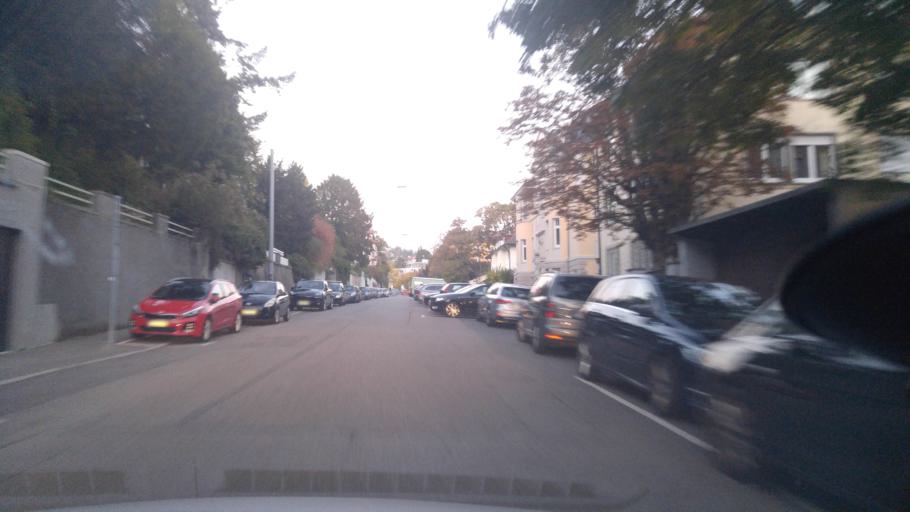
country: DE
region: Baden-Wuerttemberg
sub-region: Regierungsbezirk Stuttgart
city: Stuttgart
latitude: 48.7847
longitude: 9.1583
